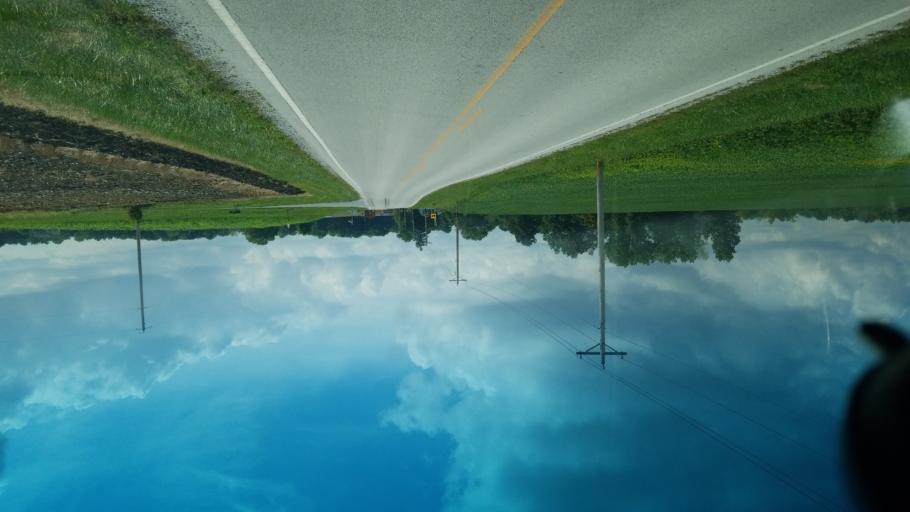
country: US
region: Ohio
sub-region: Wyandot County
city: Carey
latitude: 40.9637
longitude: -83.2790
